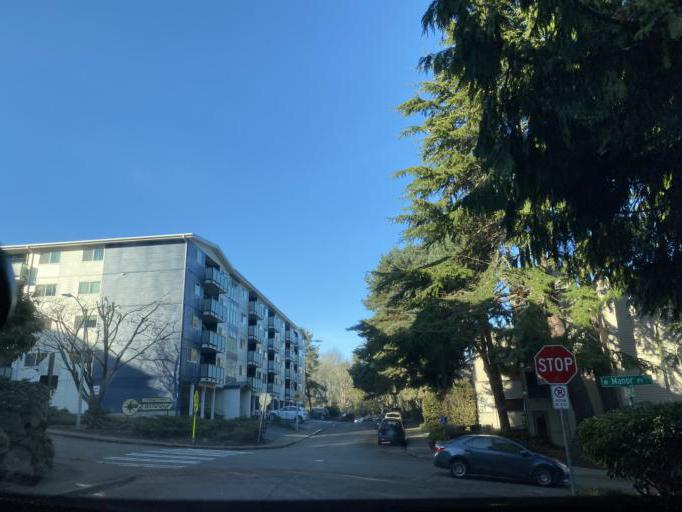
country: US
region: Washington
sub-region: King County
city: Seattle
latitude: 47.6532
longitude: -122.3900
